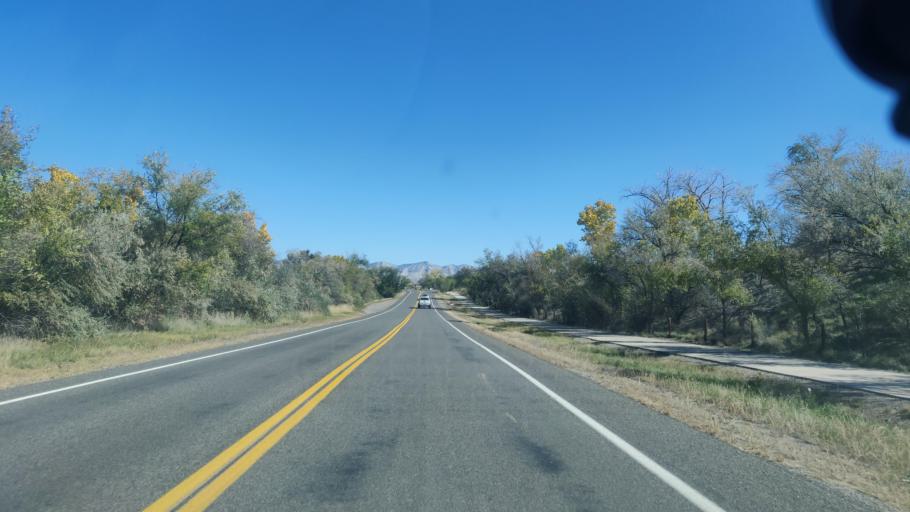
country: US
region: Colorado
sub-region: Mesa County
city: Redlands
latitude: 39.0746
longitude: -108.6385
